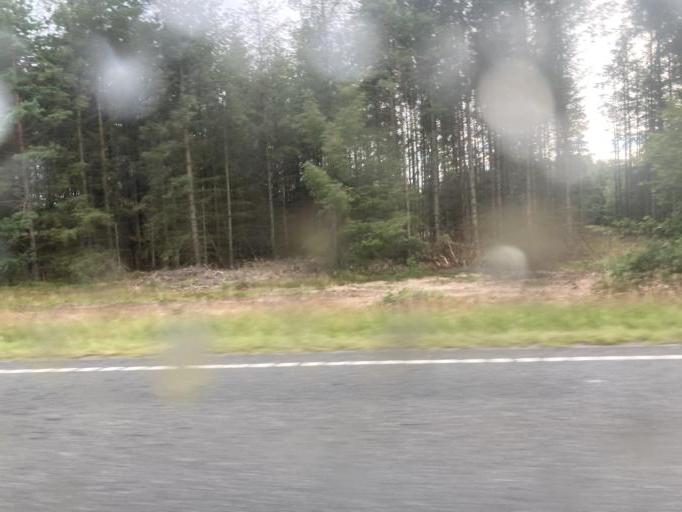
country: DK
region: South Denmark
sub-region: Varde Kommune
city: Oksbol
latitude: 55.5876
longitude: 8.2280
